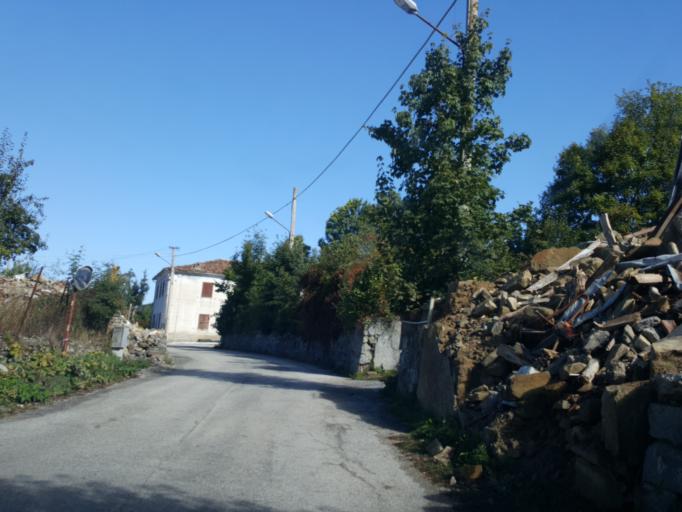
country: IT
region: Abruzzo
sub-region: Provincia dell' Aquila
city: Campotosto
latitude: 42.5644
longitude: 13.3278
